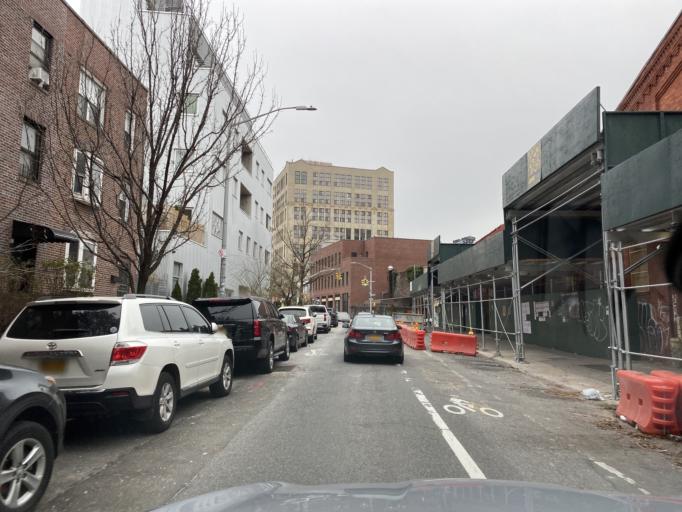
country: US
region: New York
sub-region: Queens County
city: Long Island City
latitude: 40.7162
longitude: -73.9640
